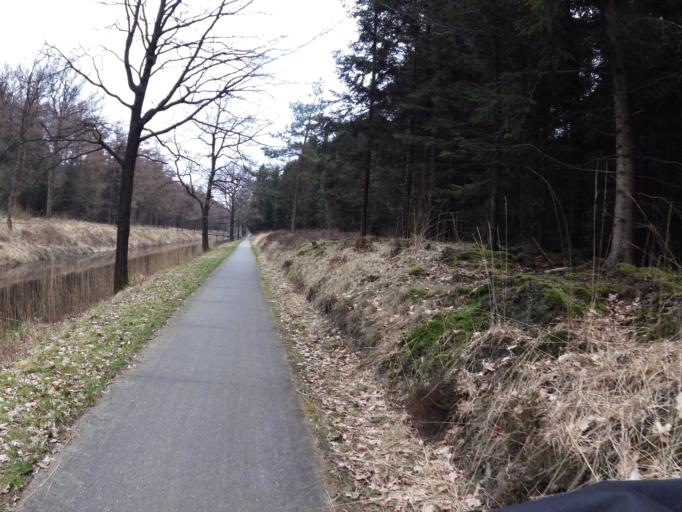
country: NL
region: Drenthe
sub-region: Gemeente Westerveld
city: Dwingeloo
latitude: 52.9763
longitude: 6.3878
